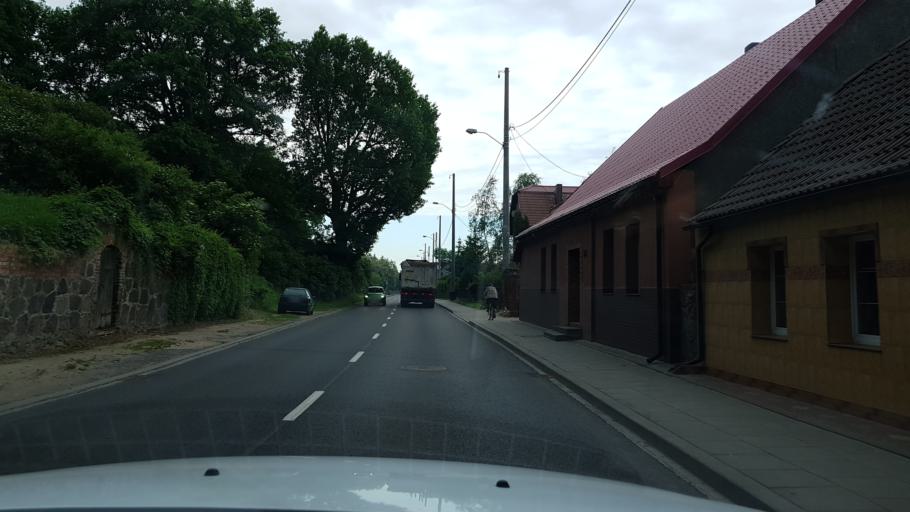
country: PL
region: West Pomeranian Voivodeship
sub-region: Powiat gryfinski
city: Gryfino
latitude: 53.3138
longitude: 14.5337
